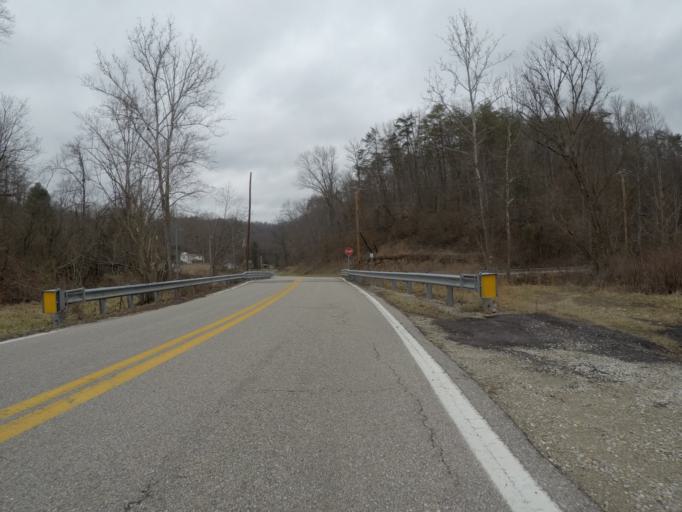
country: US
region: West Virginia
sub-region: Cabell County
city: Lesage
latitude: 38.4680
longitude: -82.2801
